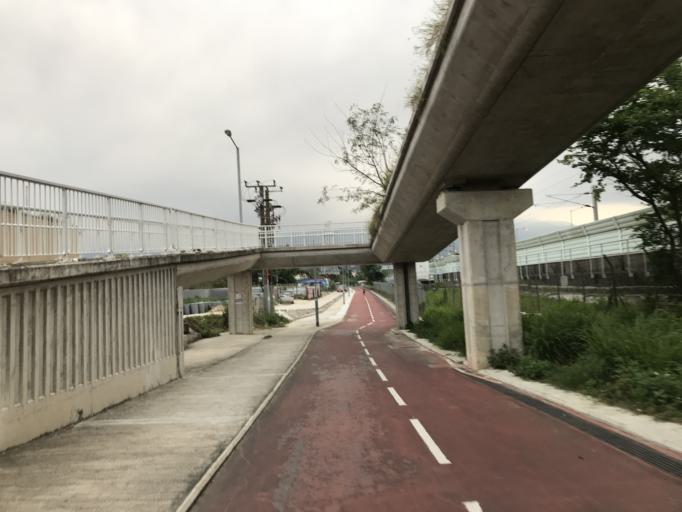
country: HK
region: Tai Po
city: Tai Po
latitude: 22.4712
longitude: 114.1537
